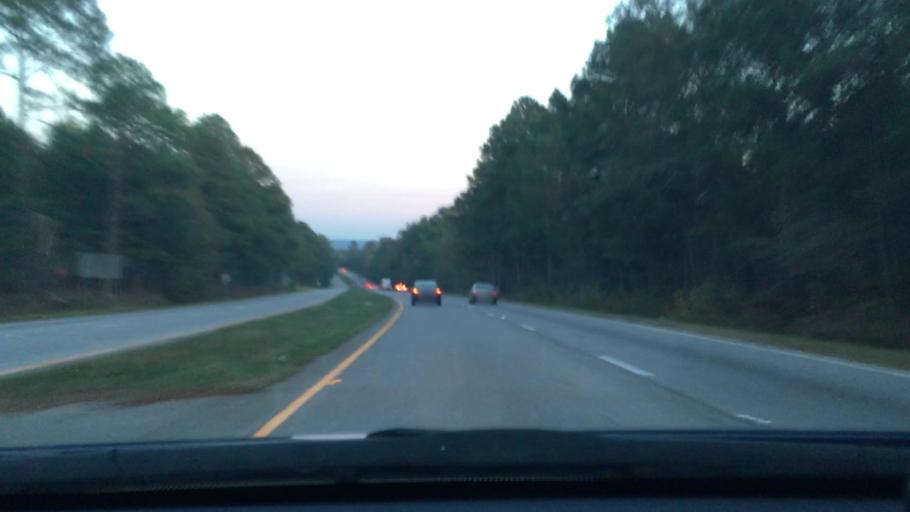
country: US
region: South Carolina
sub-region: Richland County
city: Gadsden
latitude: 33.9423
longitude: -80.6825
